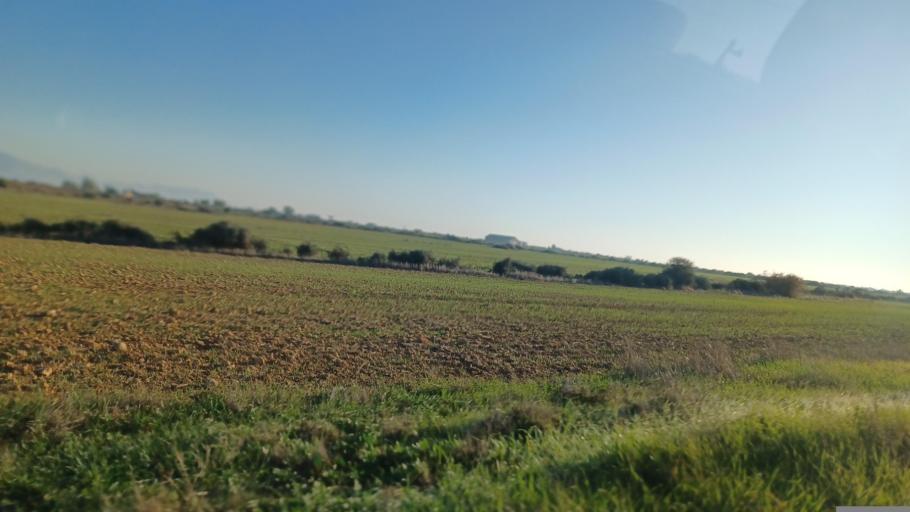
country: CY
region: Lefkosia
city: Kato Deftera
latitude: 35.1447
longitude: 33.2713
